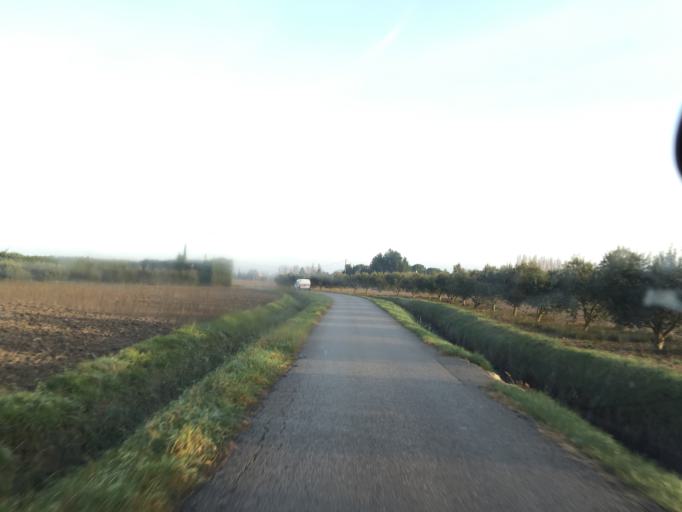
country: FR
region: Provence-Alpes-Cote d'Azur
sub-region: Departement du Vaucluse
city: Caderousse
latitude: 44.1164
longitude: 4.7633
